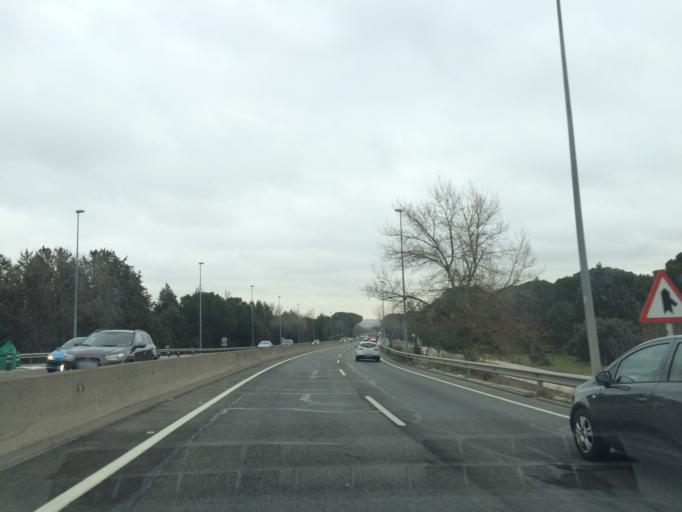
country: ES
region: Madrid
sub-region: Provincia de Madrid
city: Moncloa-Aravaca
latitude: 40.4434
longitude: -3.7494
